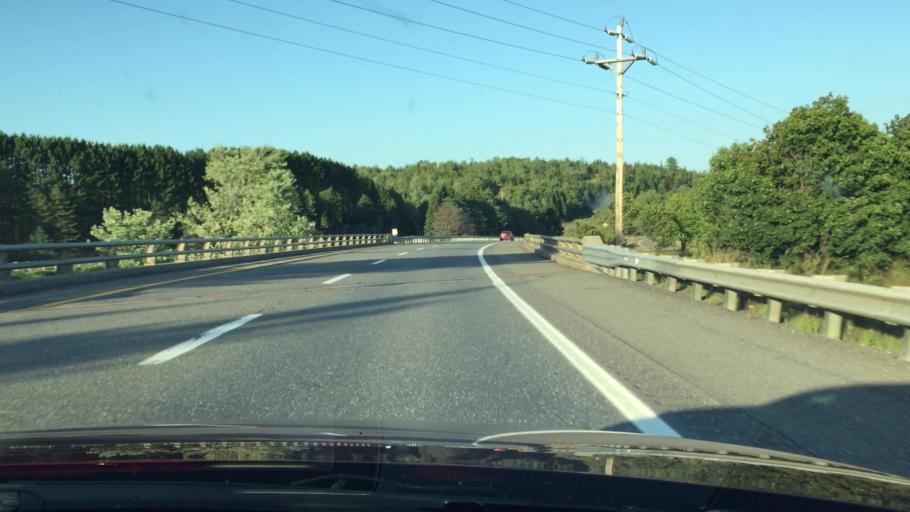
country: US
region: Maine
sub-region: Aroostook County
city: Hodgdon
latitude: 46.1445
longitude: -68.0598
